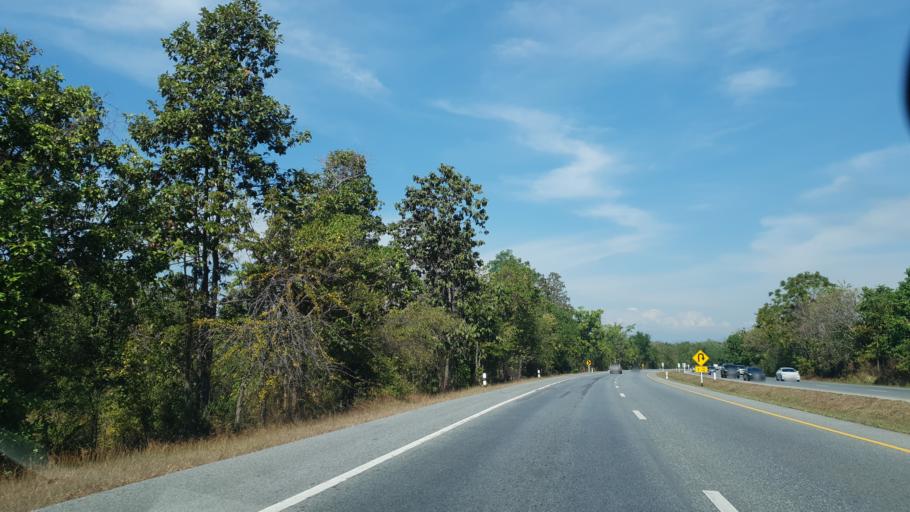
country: TH
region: Uttaradit
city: Thong Saen Khan
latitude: 17.4243
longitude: 100.2257
